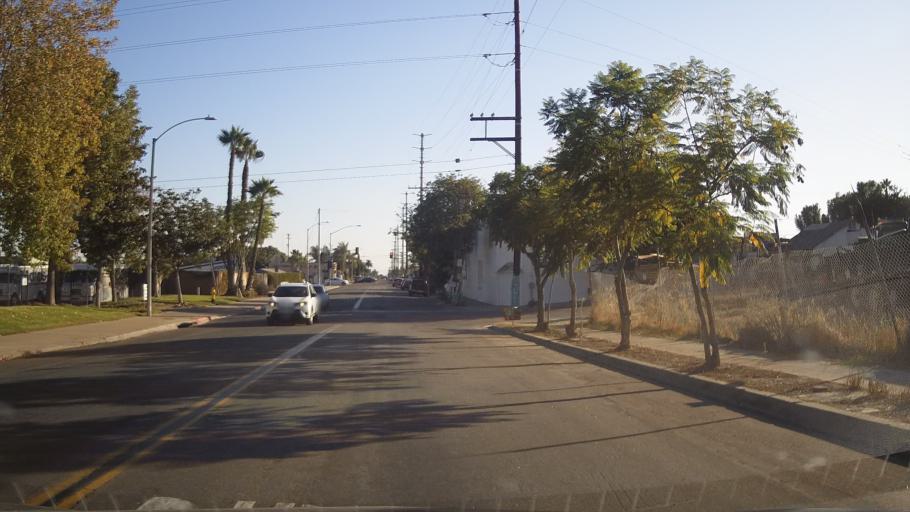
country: US
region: California
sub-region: San Diego County
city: San Diego
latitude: 32.7131
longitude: -117.1253
